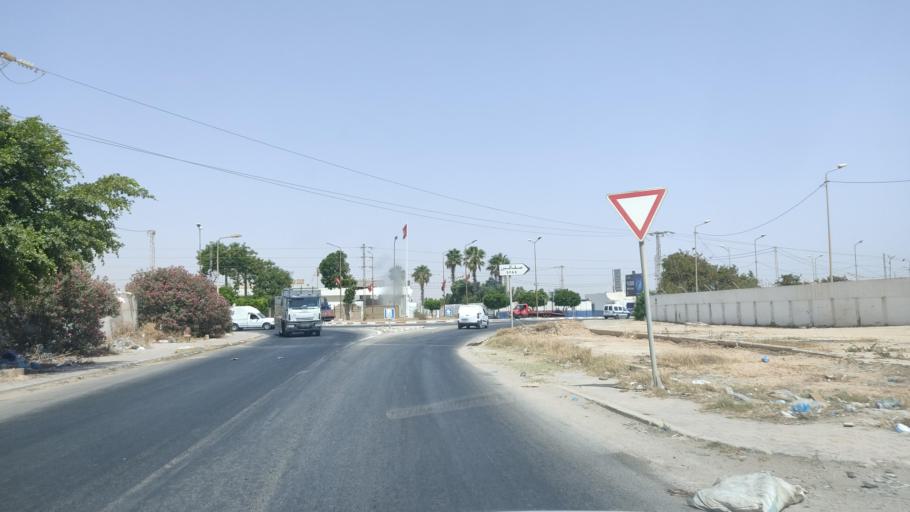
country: TN
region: Safaqis
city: Sfax
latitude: 34.6990
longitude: 10.7191
